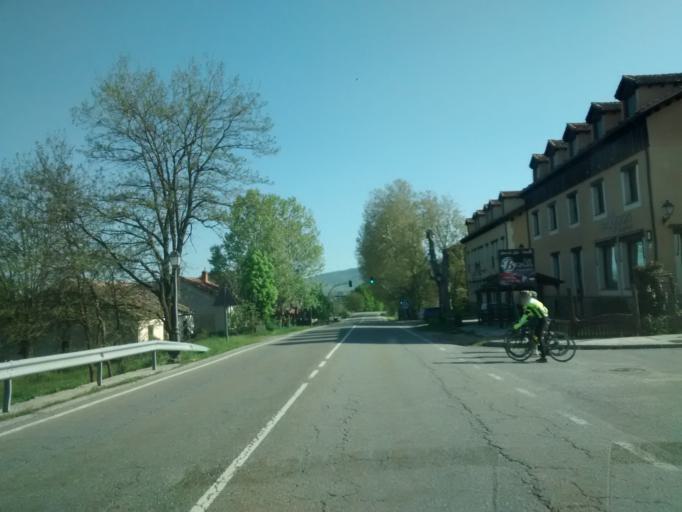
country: ES
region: Castille and Leon
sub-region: Provincia de Segovia
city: San Ildefonso
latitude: 40.8744
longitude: -4.0210
